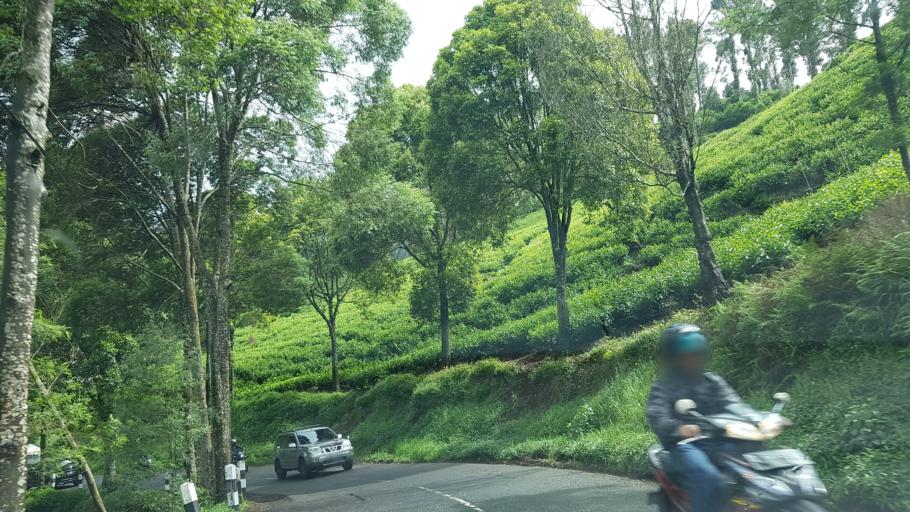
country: ID
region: West Java
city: Banjar
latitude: -7.1457
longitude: 107.3845
